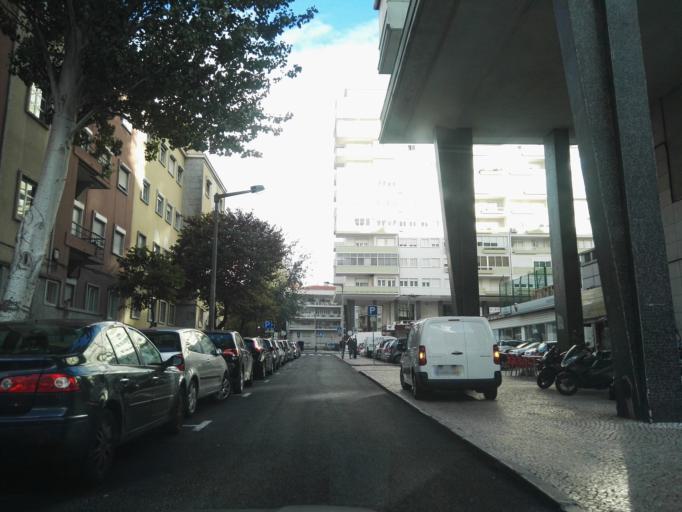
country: PT
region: Lisbon
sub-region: Lisbon
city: Lisbon
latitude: 38.7497
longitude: -9.1450
